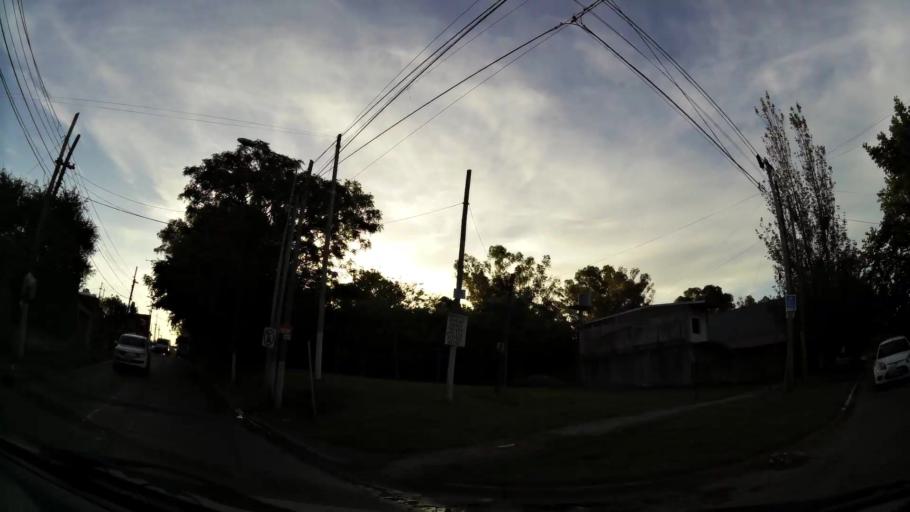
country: AR
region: Buenos Aires
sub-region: Partido de Quilmes
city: Quilmes
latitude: -34.7781
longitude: -58.1955
